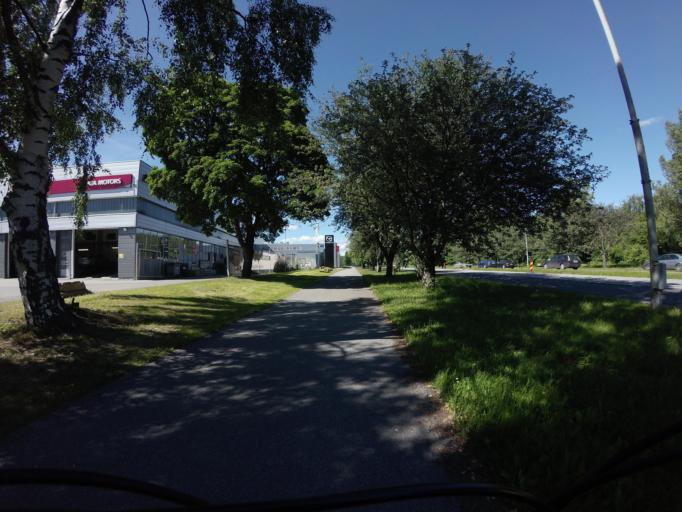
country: FI
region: Varsinais-Suomi
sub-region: Turku
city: Turku
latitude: 60.4707
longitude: 22.2655
